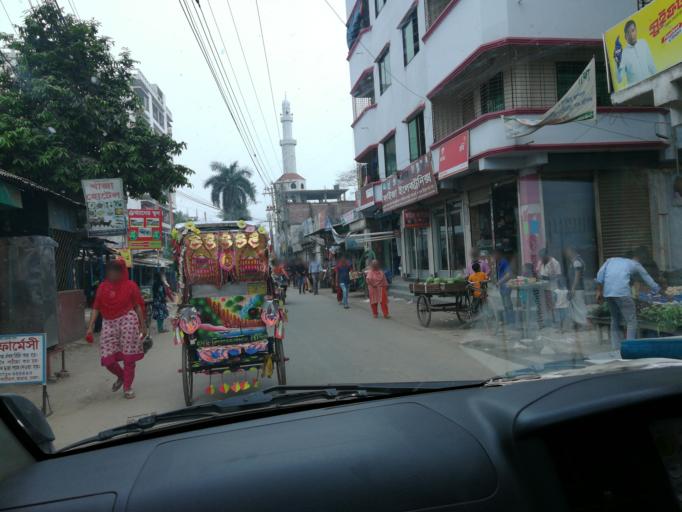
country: BD
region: Dhaka
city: Tungi
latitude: 23.8482
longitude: 90.2647
